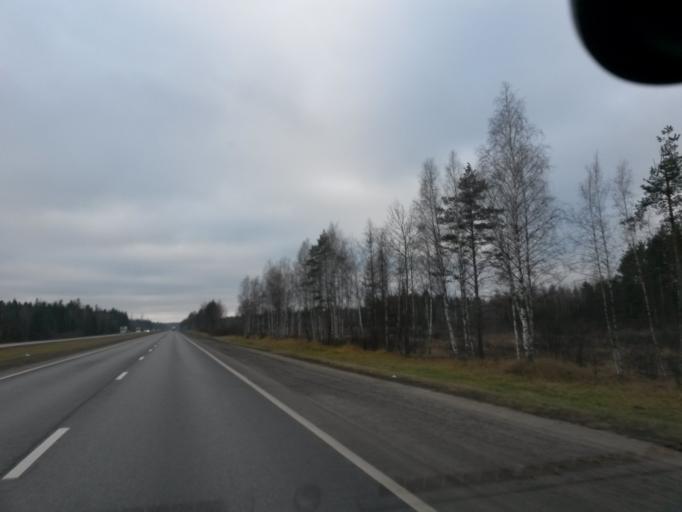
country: RU
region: Jaroslavl
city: Krasnyye Tkachi
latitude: 57.4853
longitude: 39.7756
